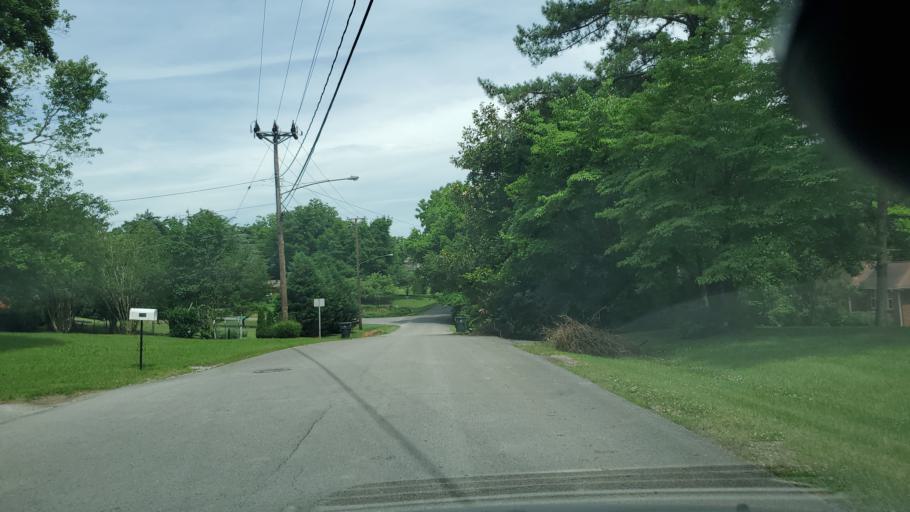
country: US
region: Tennessee
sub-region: Davidson County
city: Oak Hill
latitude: 36.1112
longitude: -86.6993
